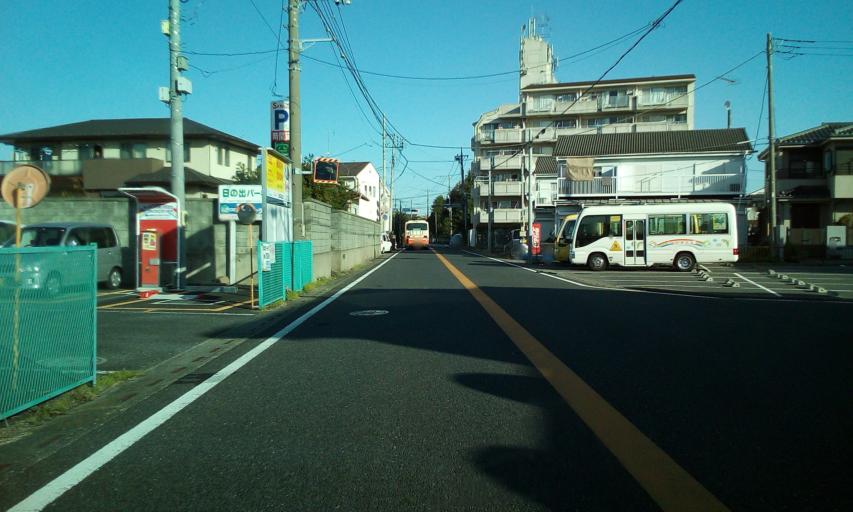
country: JP
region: Chiba
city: Nagareyama
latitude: 35.8557
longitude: 139.8902
